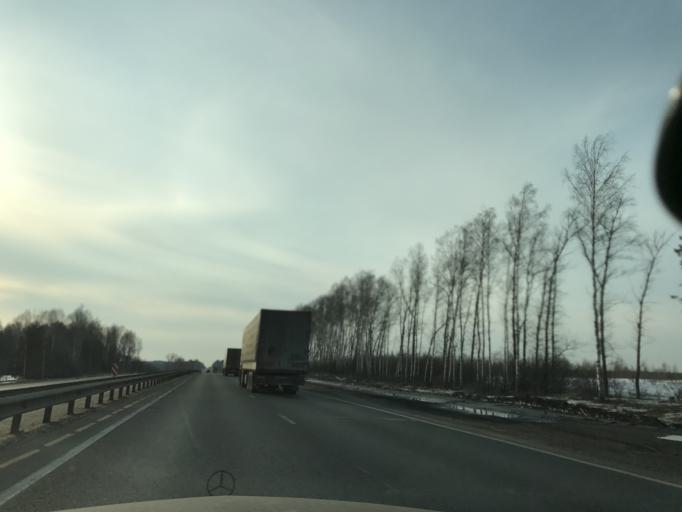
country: RU
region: Vladimir
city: Novki
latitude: 56.2028
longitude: 41.1244
